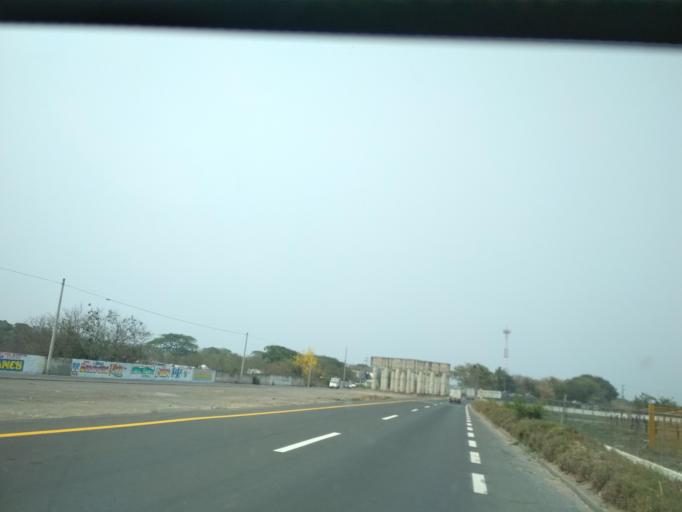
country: MX
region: Veracruz
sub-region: Veracruz
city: Delfino Victoria (Santa Fe)
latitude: 19.2014
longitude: -96.2693
